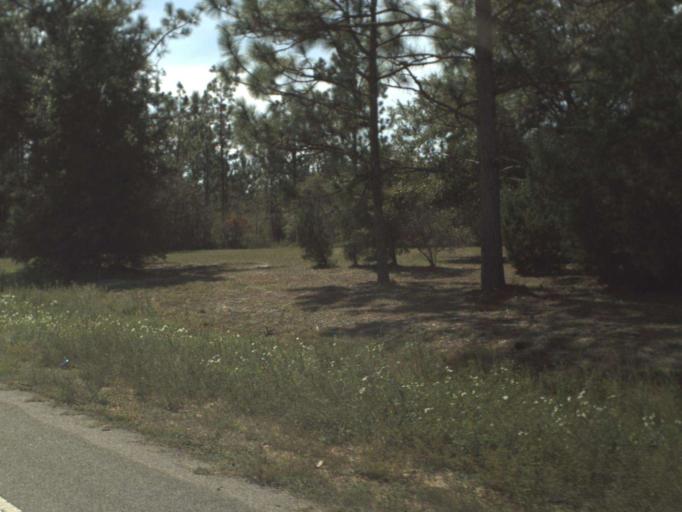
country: US
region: Florida
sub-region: Bay County
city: Lynn Haven
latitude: 30.4811
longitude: -85.6642
